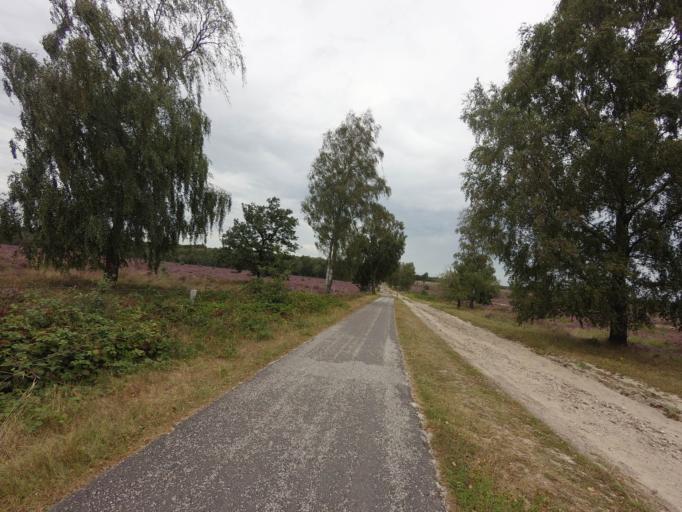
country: NL
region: Overijssel
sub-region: Gemeente Raalte
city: Raalte
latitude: 52.3457
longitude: 6.4049
